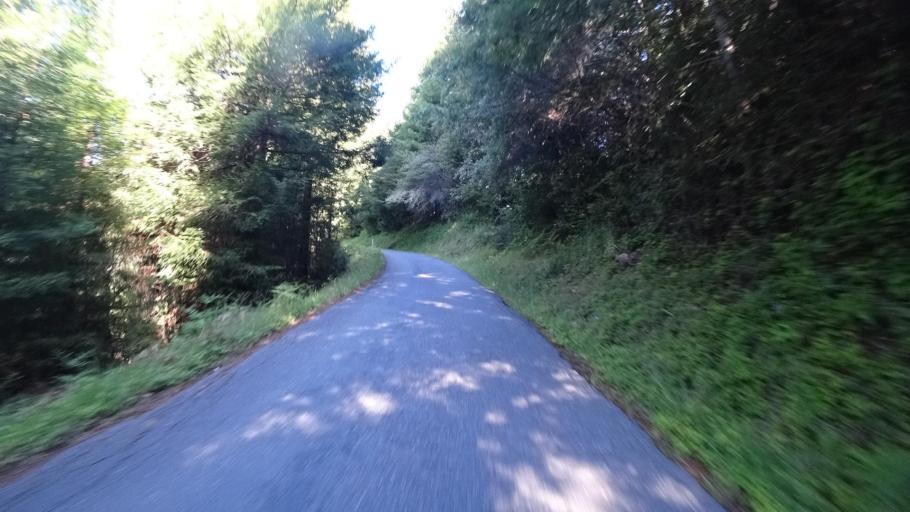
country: US
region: California
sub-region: Humboldt County
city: Rio Dell
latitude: 40.4490
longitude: -123.9777
